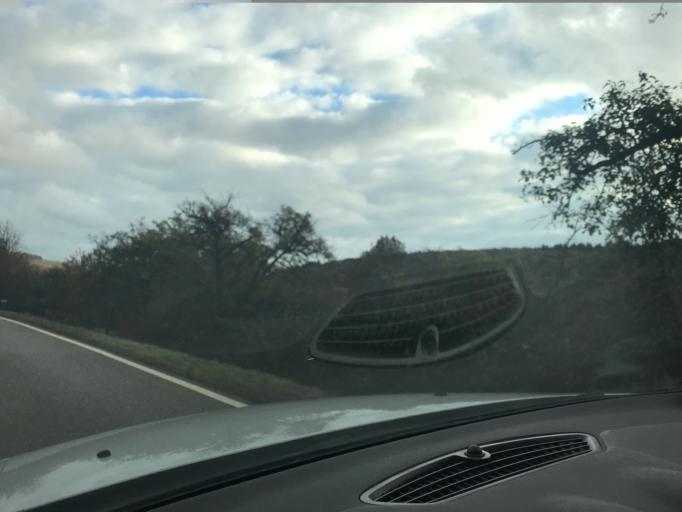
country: DE
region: Baden-Wuerttemberg
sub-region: Regierungsbezirk Stuttgart
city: Grossbottwar
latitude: 49.0020
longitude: 9.2752
